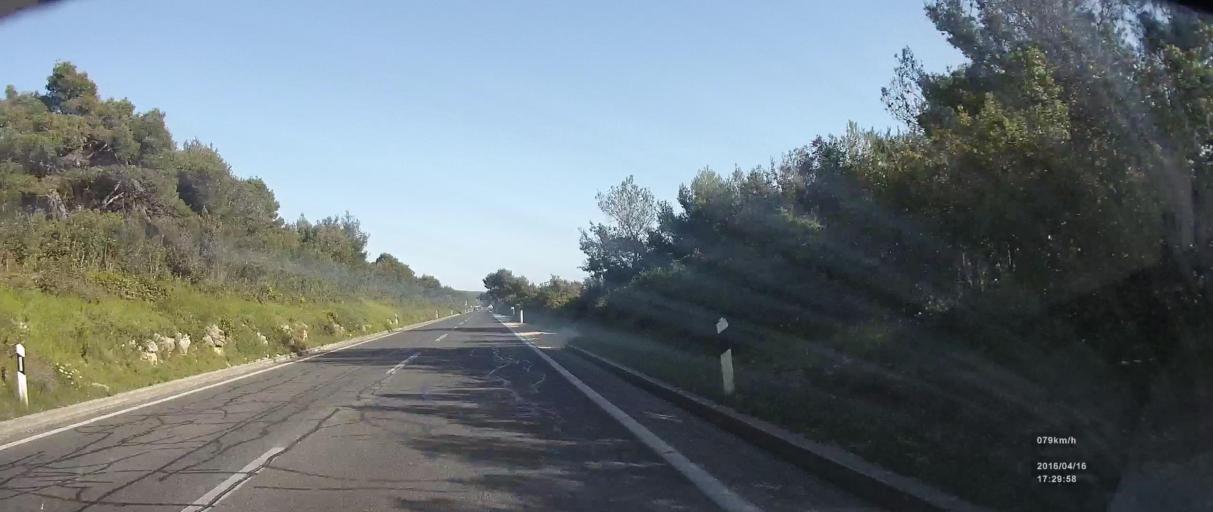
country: HR
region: Zadarska
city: Sukosan
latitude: 44.0263
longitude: 15.3484
